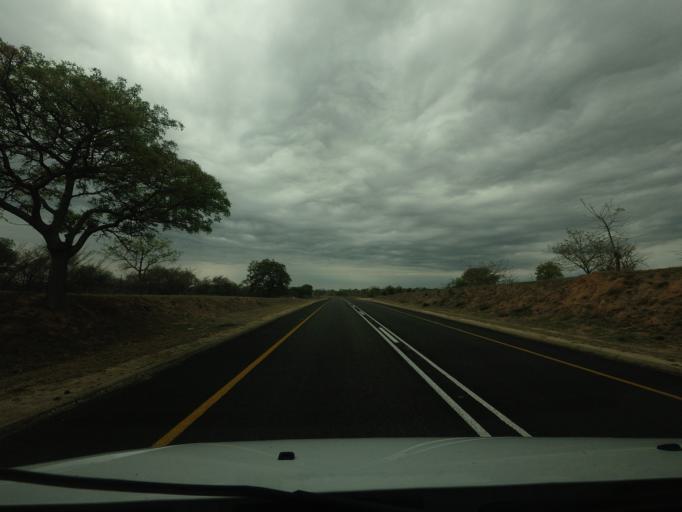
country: ZA
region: Limpopo
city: Thulamahashi
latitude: -24.5686
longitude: 31.0659
